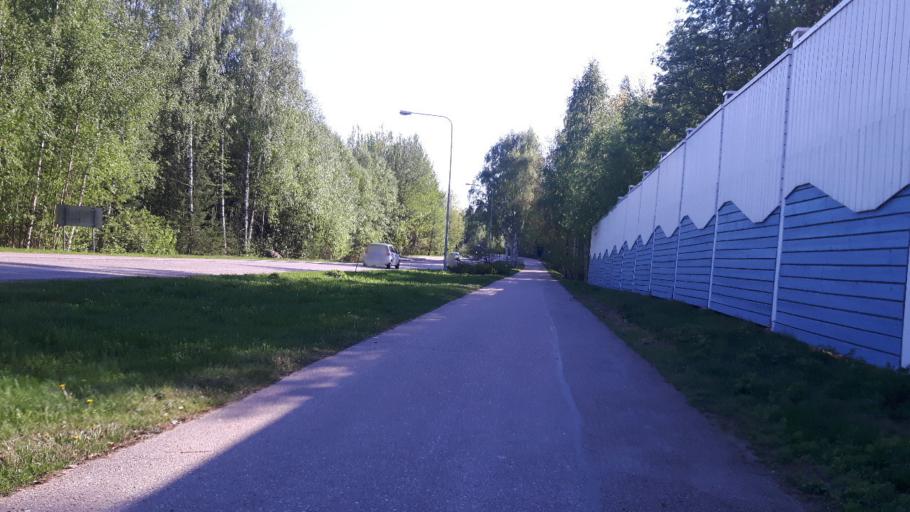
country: FI
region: Kymenlaakso
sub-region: Kotka-Hamina
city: Kotka
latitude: 60.4391
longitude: 26.8833
